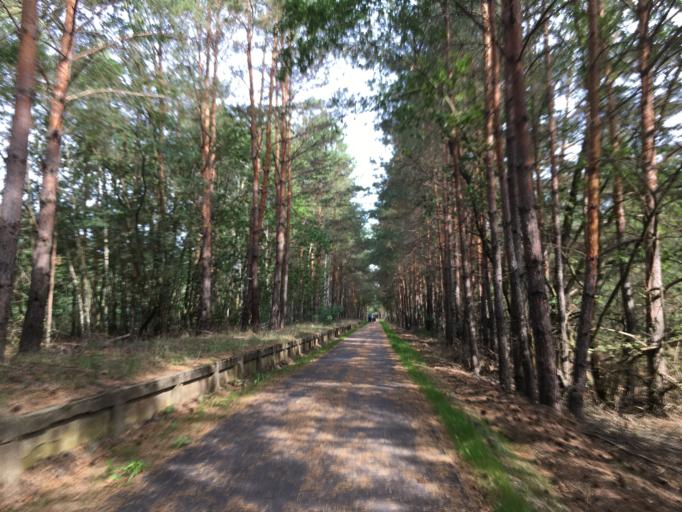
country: DE
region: Brandenburg
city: Heinersbruck
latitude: 51.8261
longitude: 14.5844
